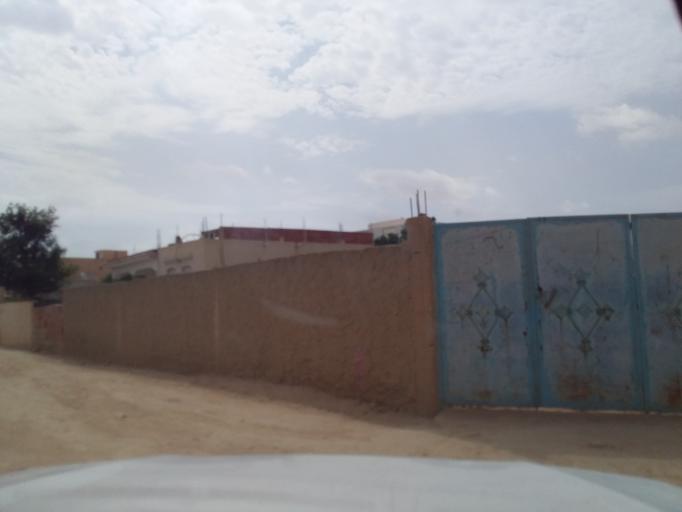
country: TN
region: Qabis
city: Matmata
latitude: 33.6148
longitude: 10.2921
